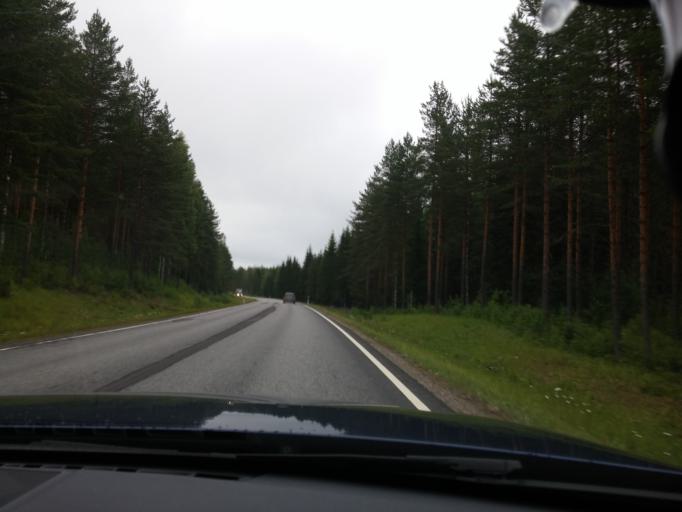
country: FI
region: Pirkanmaa
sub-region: Ylae-Pirkanmaa
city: Maenttae
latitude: 61.9589
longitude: 24.5832
